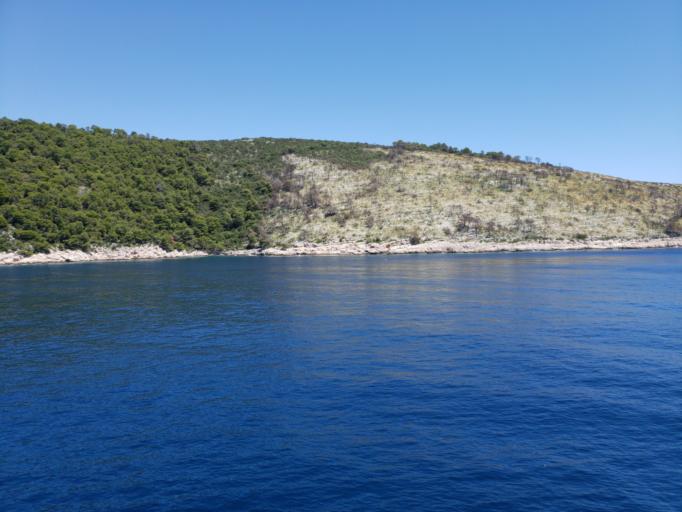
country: HR
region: Splitsko-Dalmatinska
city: Stari Grad
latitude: 43.2158
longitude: 16.5254
